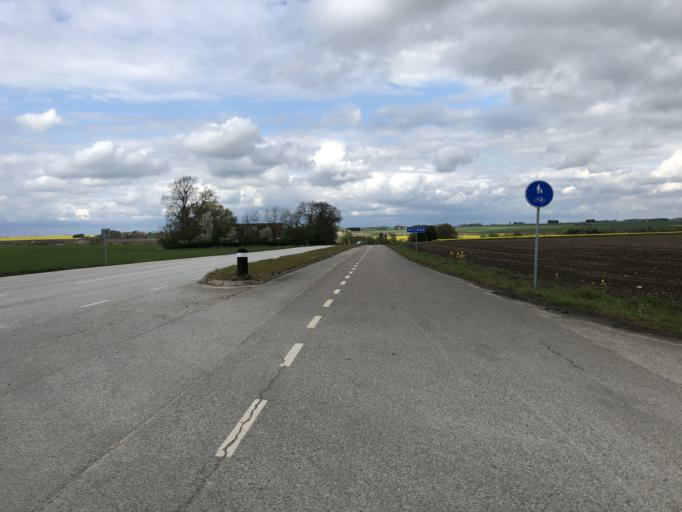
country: SE
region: Skane
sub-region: Eslovs Kommun
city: Eslov
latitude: 55.7593
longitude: 13.3062
